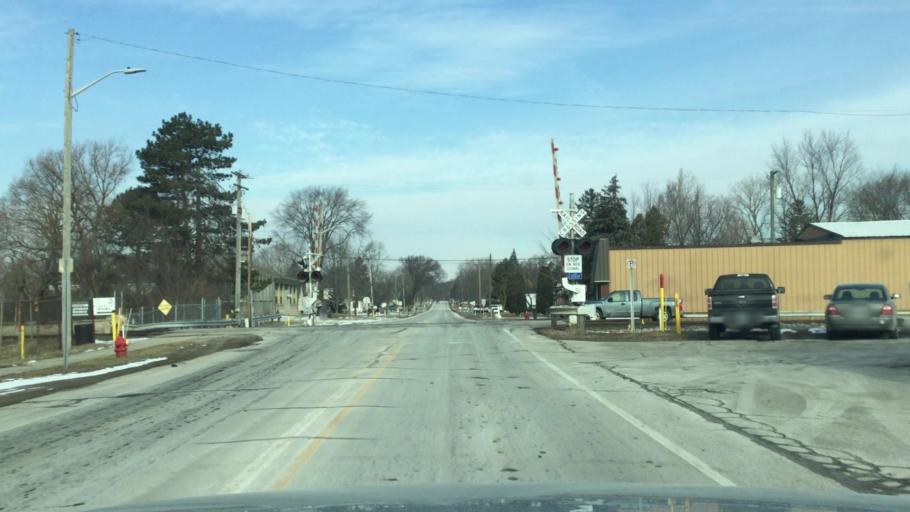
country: US
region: Michigan
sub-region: Wayne County
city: Flat Rock
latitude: 42.1001
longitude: -83.2944
